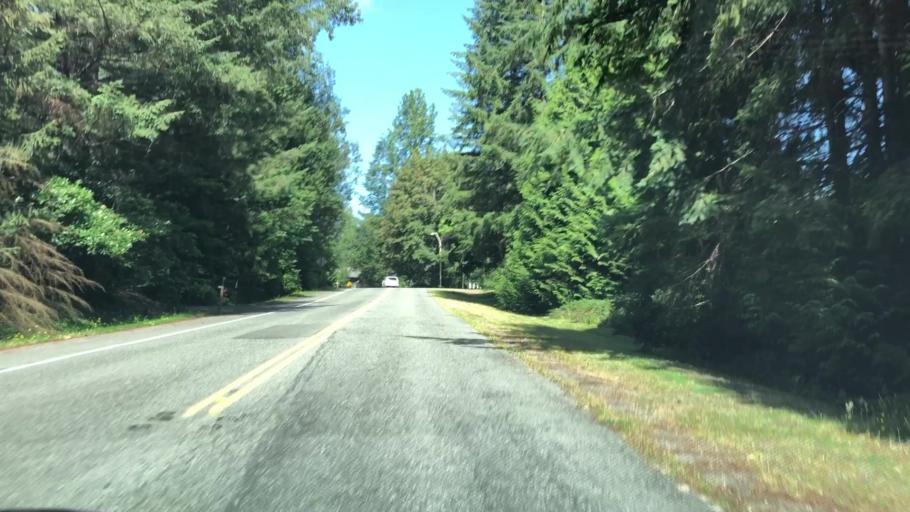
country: US
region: Washington
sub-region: King County
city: Cottage Lake
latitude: 47.7344
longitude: -122.0849
